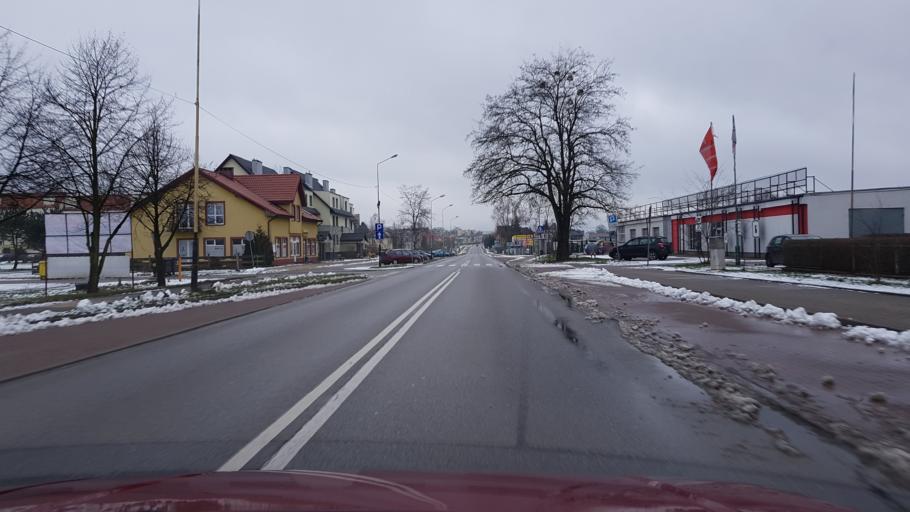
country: PL
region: West Pomeranian Voivodeship
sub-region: Powiat goleniowski
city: Nowogard
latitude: 53.6638
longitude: 15.1444
